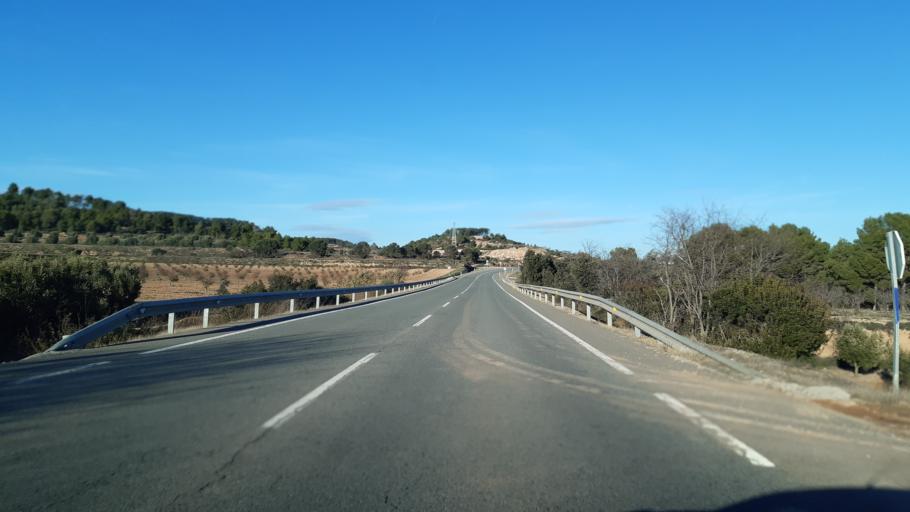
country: ES
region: Catalonia
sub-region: Provincia de Tarragona
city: la Fatarella
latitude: 41.0946
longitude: 0.5157
